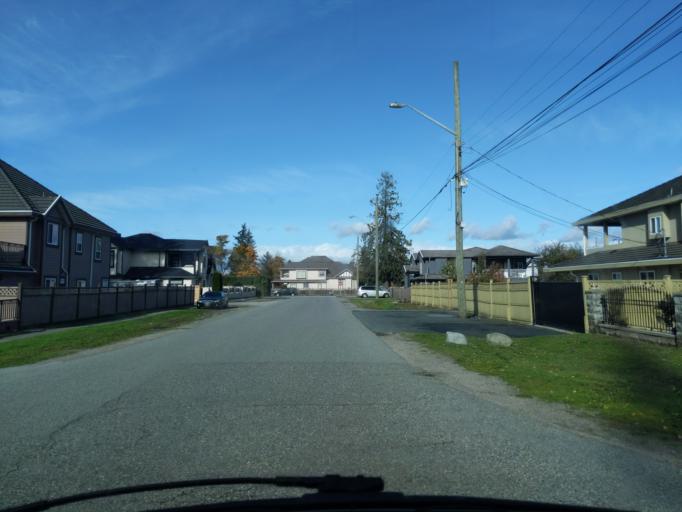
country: CA
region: British Columbia
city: New Westminster
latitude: 49.1980
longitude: -122.8624
